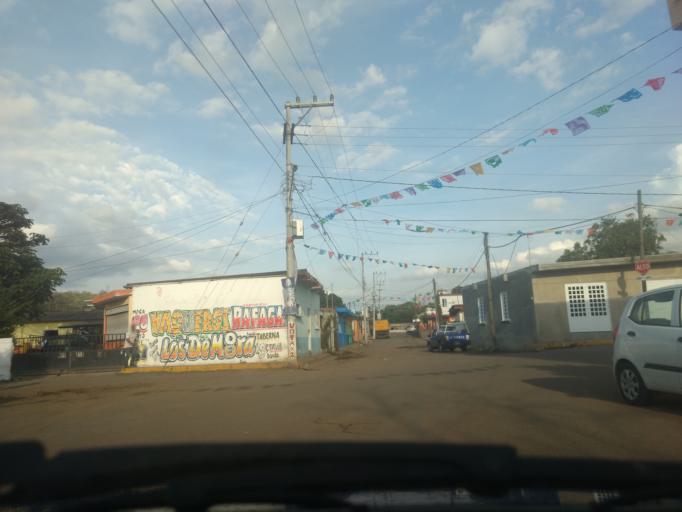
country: MX
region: Nayarit
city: Puga
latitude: 21.5266
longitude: -104.8074
